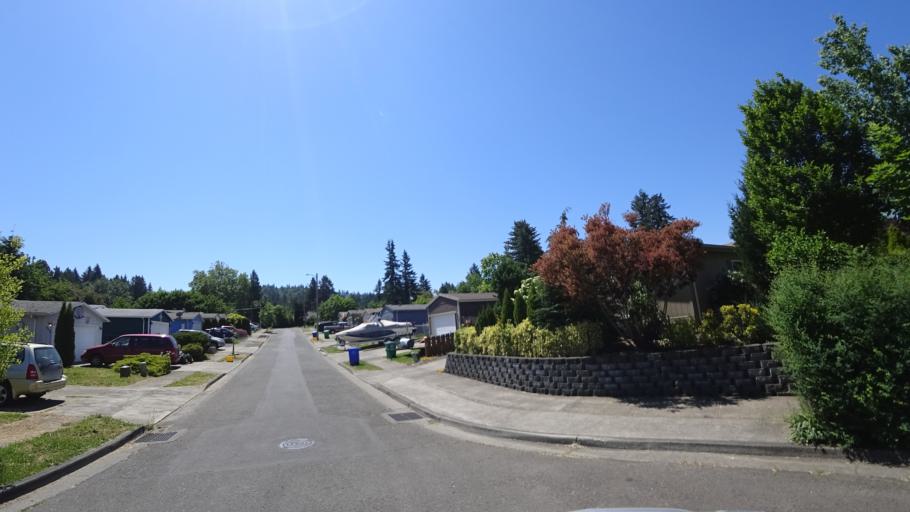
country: US
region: Oregon
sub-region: Clackamas County
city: Happy Valley
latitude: 45.4781
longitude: -122.5168
